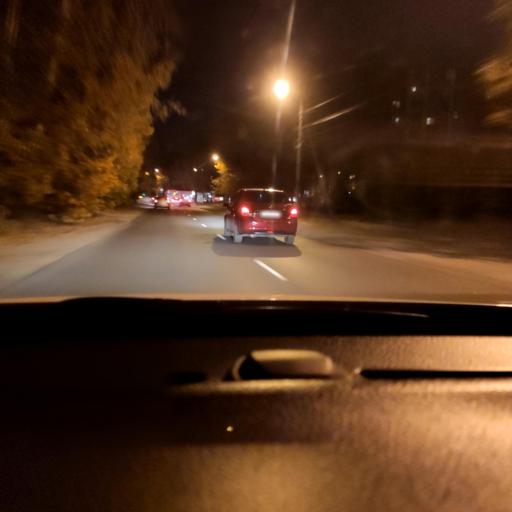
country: RU
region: Voronezj
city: Voronezh
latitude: 51.7230
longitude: 39.2172
